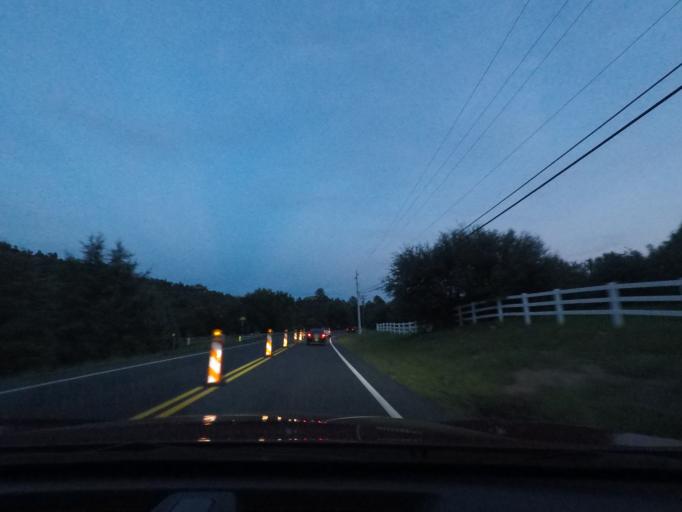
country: US
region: Arizona
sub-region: Yavapai County
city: Prescott
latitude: 34.5762
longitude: -112.5167
